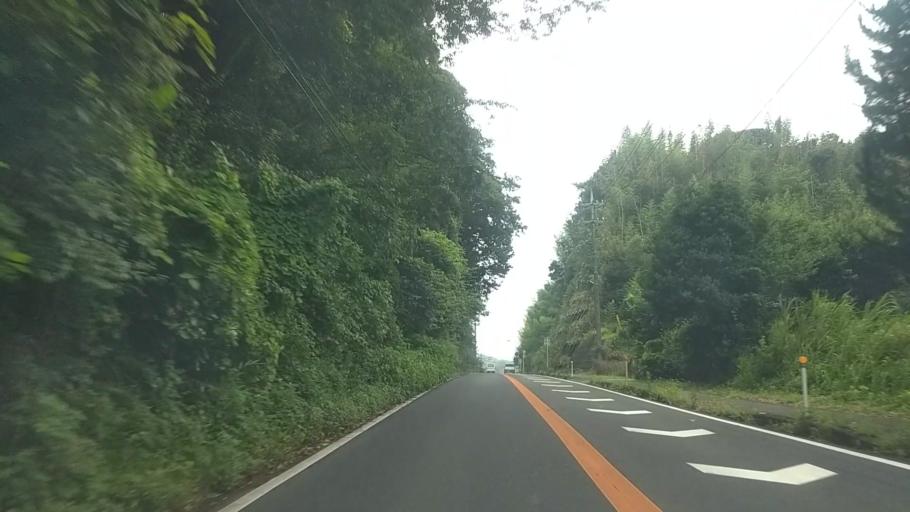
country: JP
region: Chiba
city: Kisarazu
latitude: 35.2848
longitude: 140.0808
